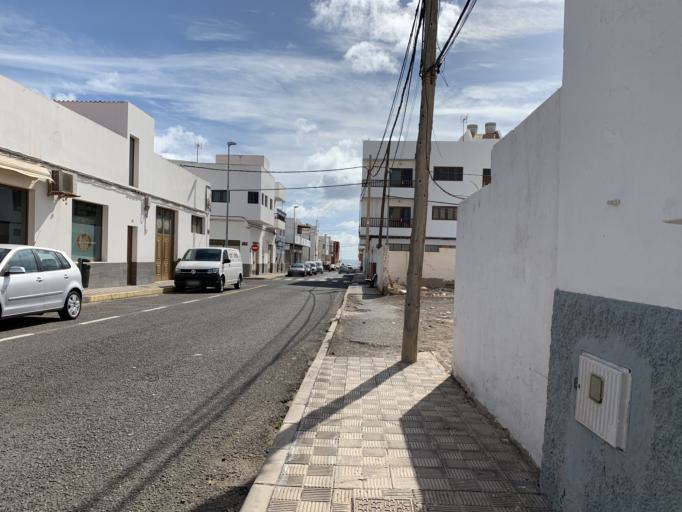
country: ES
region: Canary Islands
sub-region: Provincia de Las Palmas
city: Puerto del Rosario
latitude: 28.5041
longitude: -13.8494
